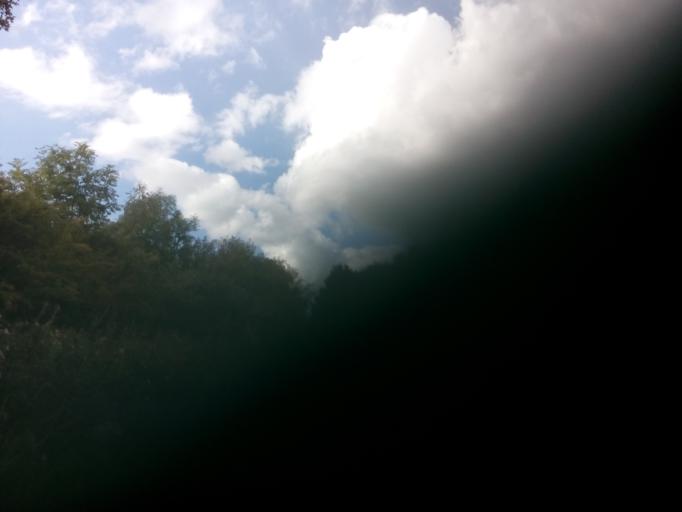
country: GB
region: England
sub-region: County Durham
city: Pittington
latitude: 54.7856
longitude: -1.5143
